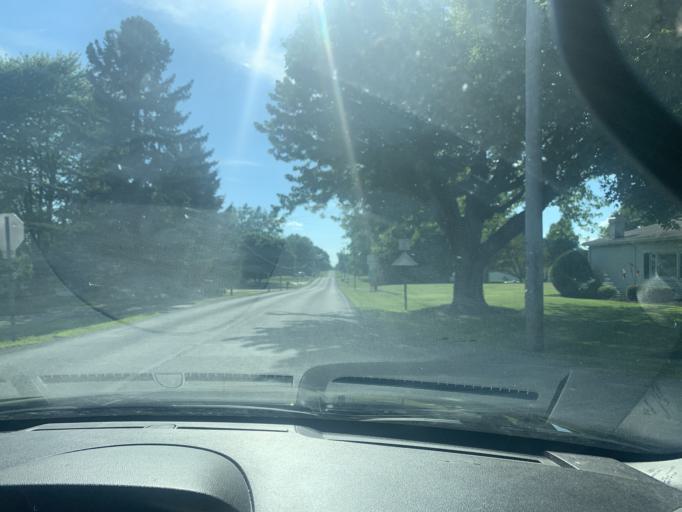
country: US
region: Ohio
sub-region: Logan County
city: Bellefontaine
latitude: 40.3487
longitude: -83.7937
